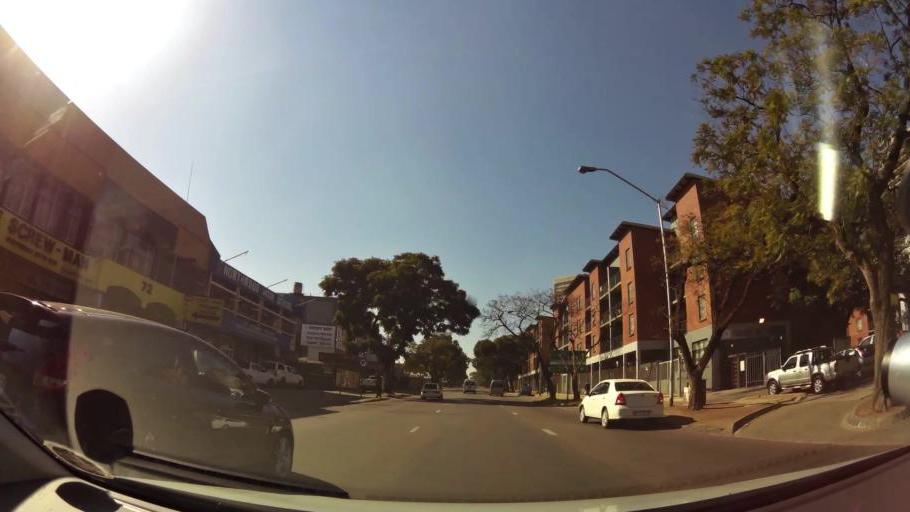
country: ZA
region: Gauteng
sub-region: City of Tshwane Metropolitan Municipality
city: Pretoria
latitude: -25.7425
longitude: 28.1814
